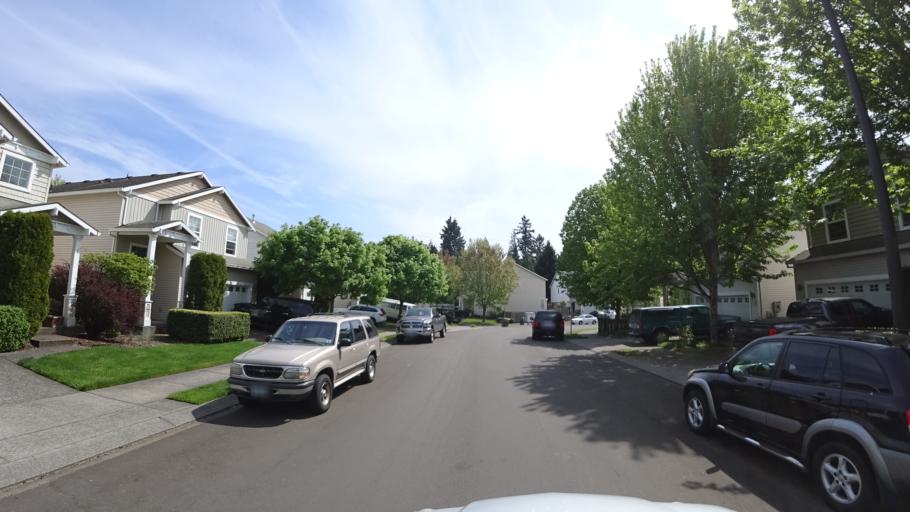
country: US
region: Oregon
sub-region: Washington County
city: Hillsboro
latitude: 45.5208
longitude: -122.9297
